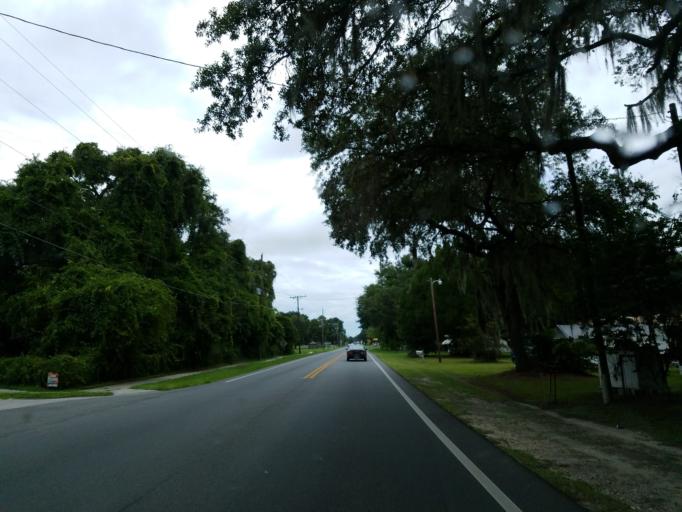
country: US
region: Florida
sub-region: Sumter County
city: Lake Panasoffkee
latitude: 28.7687
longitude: -82.1191
